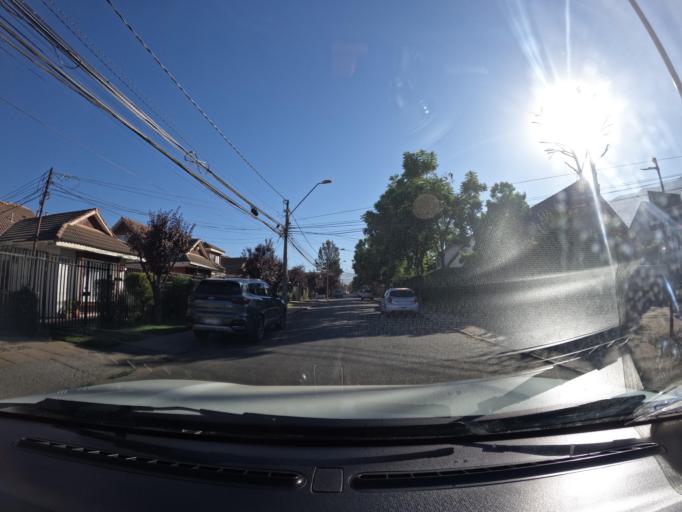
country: CL
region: Santiago Metropolitan
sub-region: Provincia de Santiago
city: Villa Presidente Frei, Nunoa, Santiago, Chile
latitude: -33.4806
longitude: -70.5500
